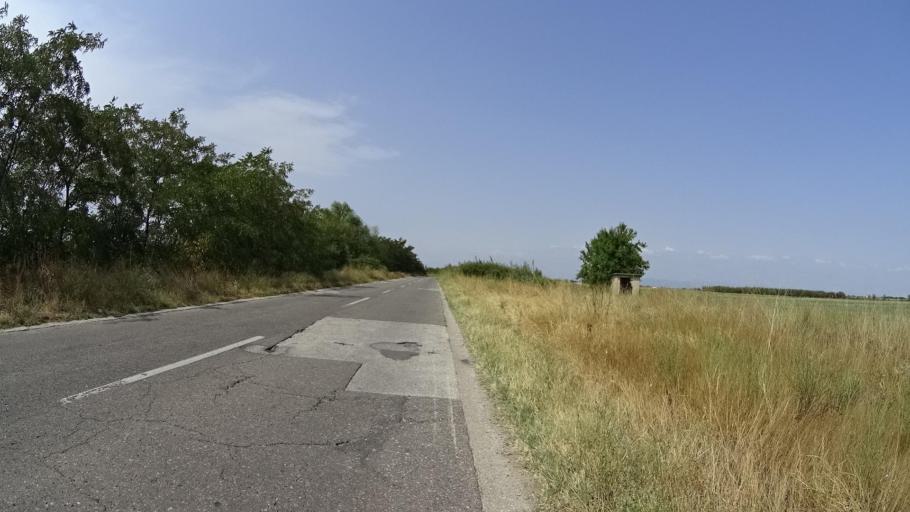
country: BG
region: Plovdiv
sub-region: Obshtina Plovdiv
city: Plovdiv
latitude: 42.2233
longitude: 24.7855
